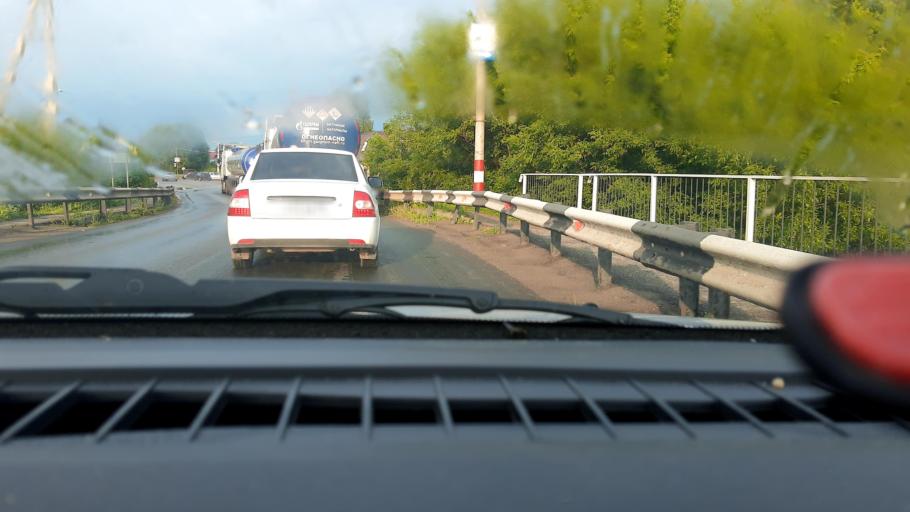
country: RU
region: Nizjnij Novgorod
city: Lukoyanov
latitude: 55.0296
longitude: 44.4904
